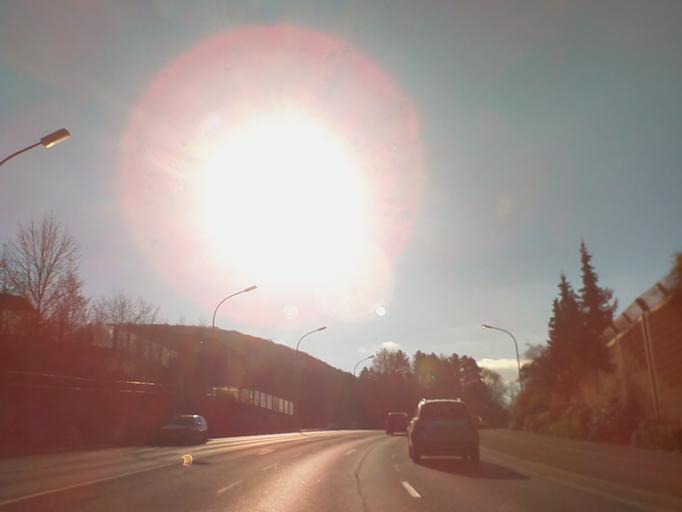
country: DE
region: Bavaria
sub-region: Regierungsbezirk Unterfranken
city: Bad Kissingen
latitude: 50.2025
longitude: 10.0894
